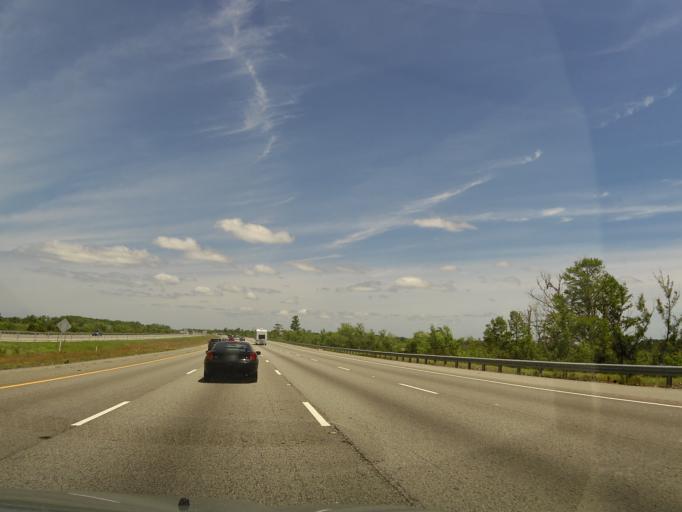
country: US
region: Georgia
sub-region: McIntosh County
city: Darien
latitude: 31.3405
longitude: -81.4647
